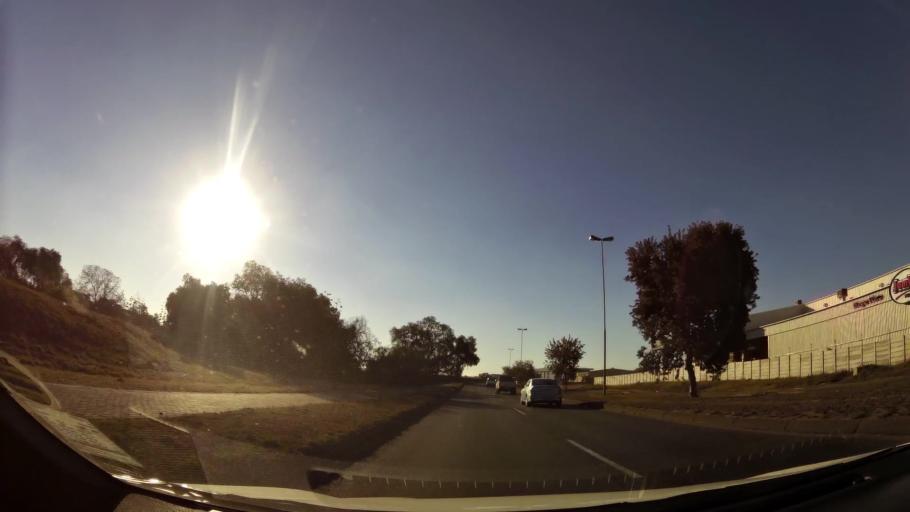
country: ZA
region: Limpopo
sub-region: Capricorn District Municipality
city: Polokwane
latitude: -23.8969
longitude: 29.4384
